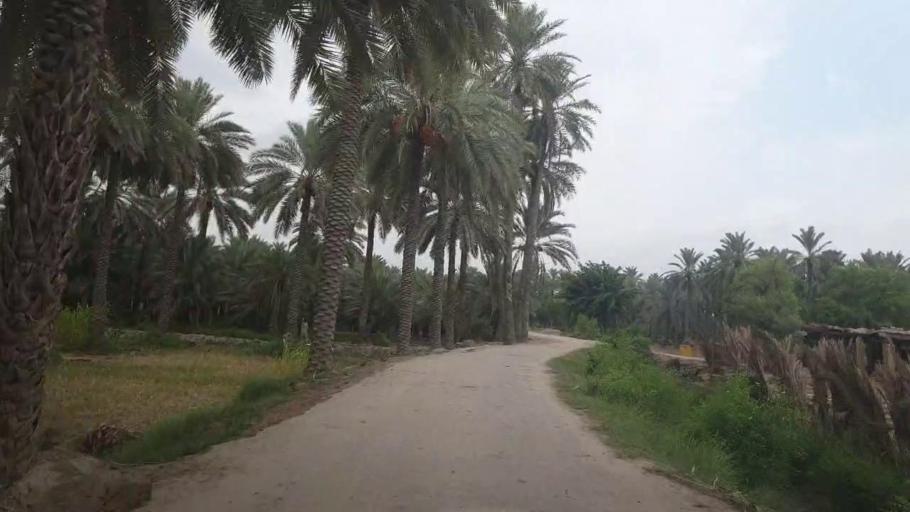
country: PK
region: Sindh
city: Khairpur
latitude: 27.5813
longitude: 68.7111
